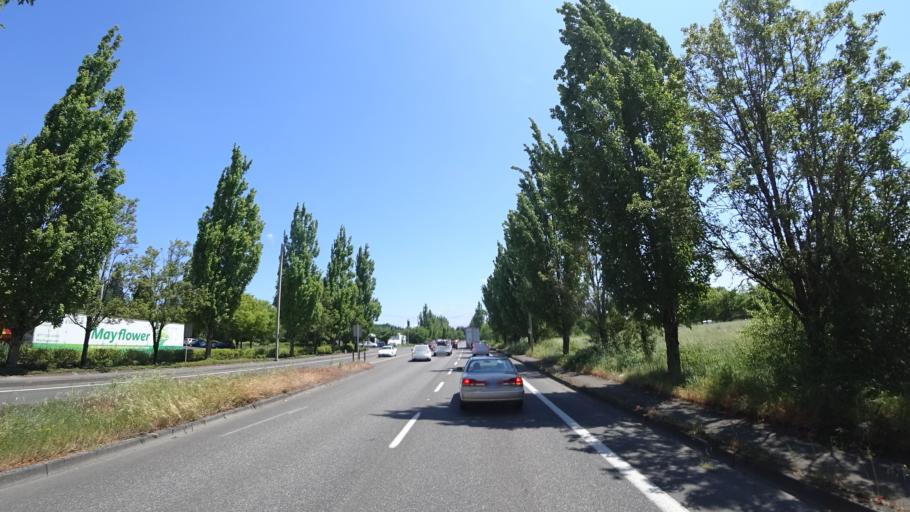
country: US
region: Oregon
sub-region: Multnomah County
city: Fairview
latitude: 45.5578
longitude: -122.5018
